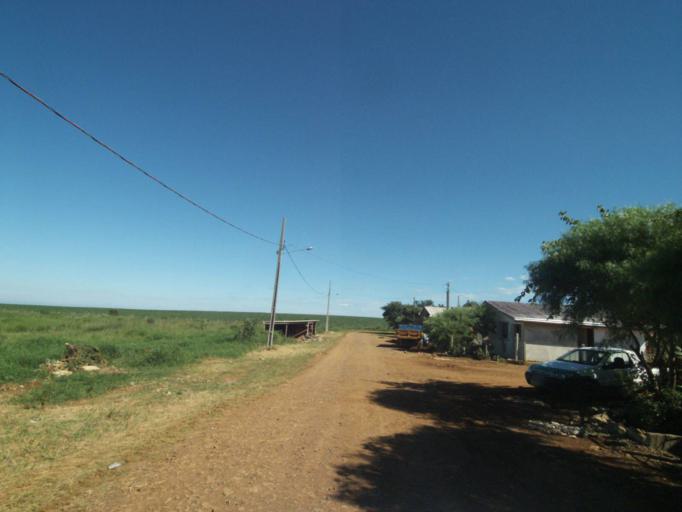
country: BR
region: Parana
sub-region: Pinhao
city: Pinhao
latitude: -25.8349
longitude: -52.0337
